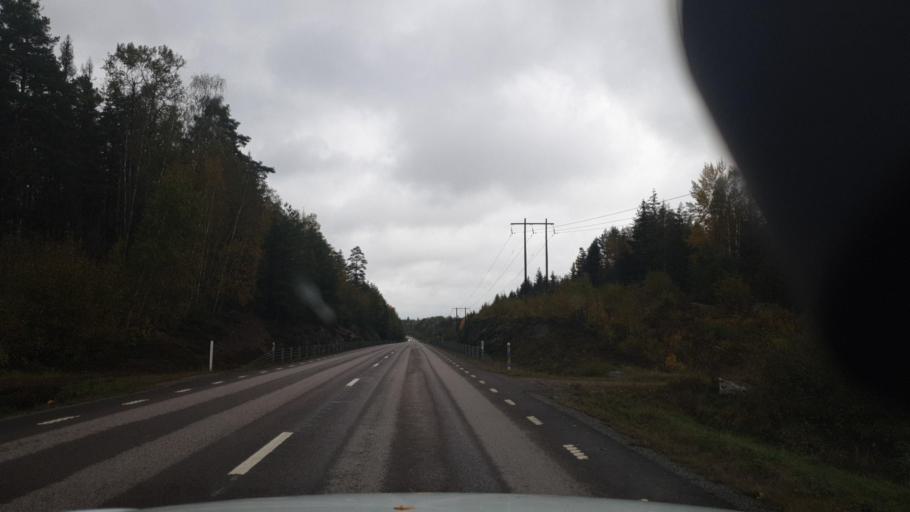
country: SE
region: Vaermland
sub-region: Karlstads Kommun
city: Edsvalla
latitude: 59.4197
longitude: 13.1892
